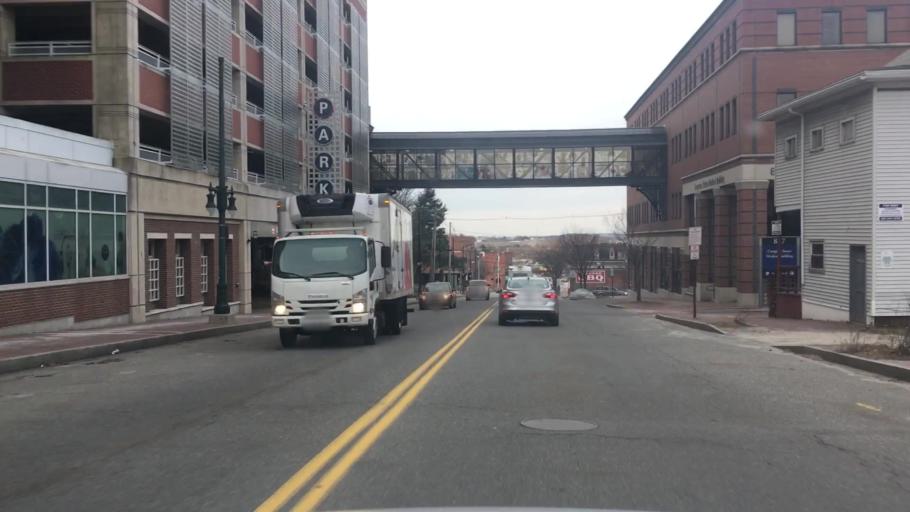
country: US
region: Maine
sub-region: Cumberland County
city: Portland
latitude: 43.6546
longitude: -70.2760
